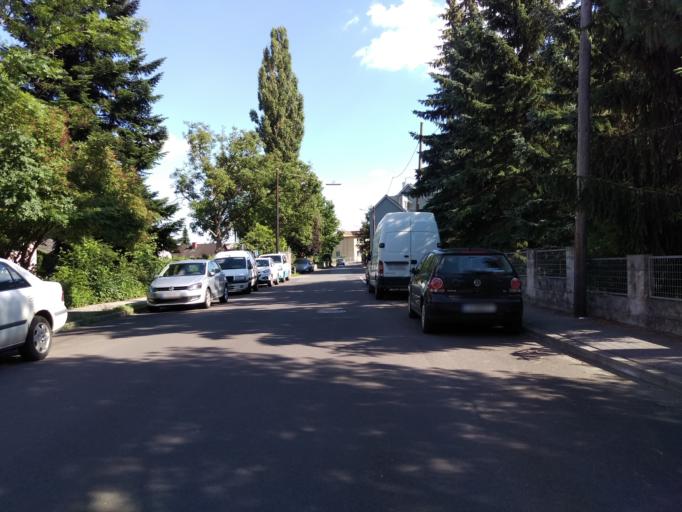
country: AT
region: Styria
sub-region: Graz Stadt
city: Wetzelsdorf
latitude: 47.0606
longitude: 15.3900
